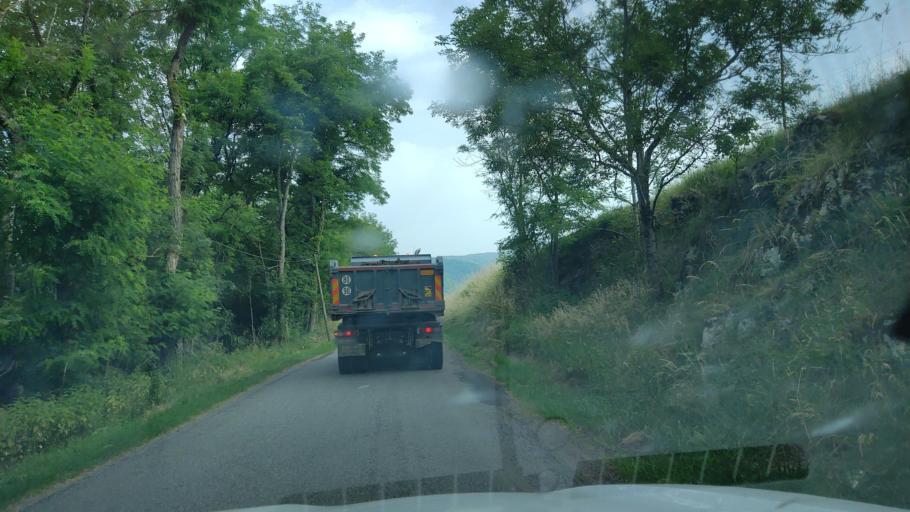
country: FR
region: Rhone-Alpes
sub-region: Departement de la Savoie
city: Barby
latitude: 45.5738
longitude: 6.0307
